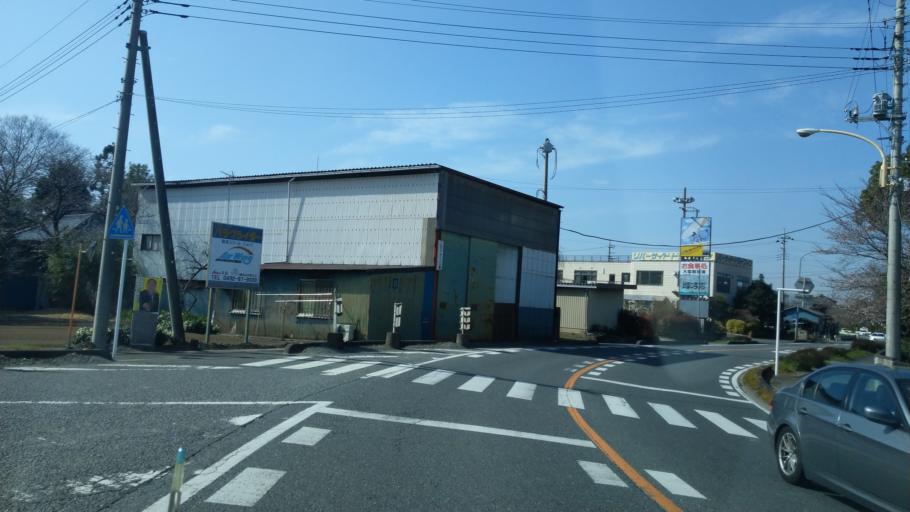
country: JP
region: Saitama
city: Okegawa
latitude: 35.9533
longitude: 139.5299
